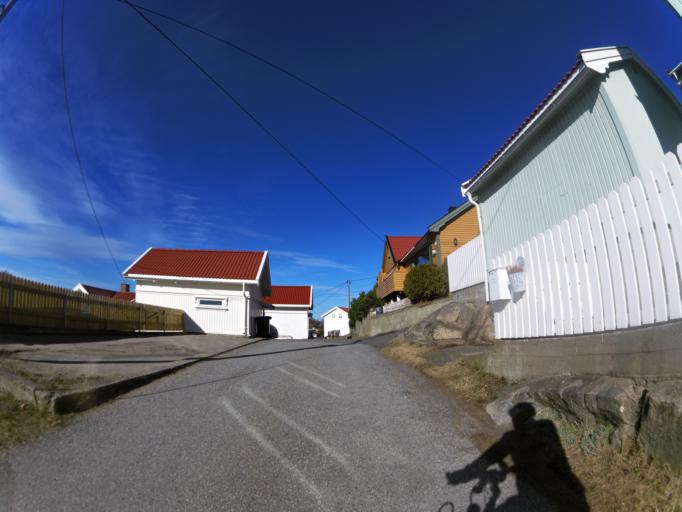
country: NO
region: Ostfold
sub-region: Fredrikstad
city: Fredrikstad
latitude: 59.2107
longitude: 10.9012
